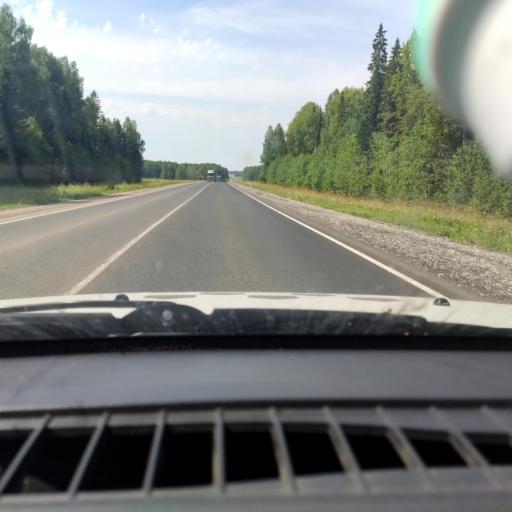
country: RU
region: Perm
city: Siva
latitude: 58.3954
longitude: 54.5189
